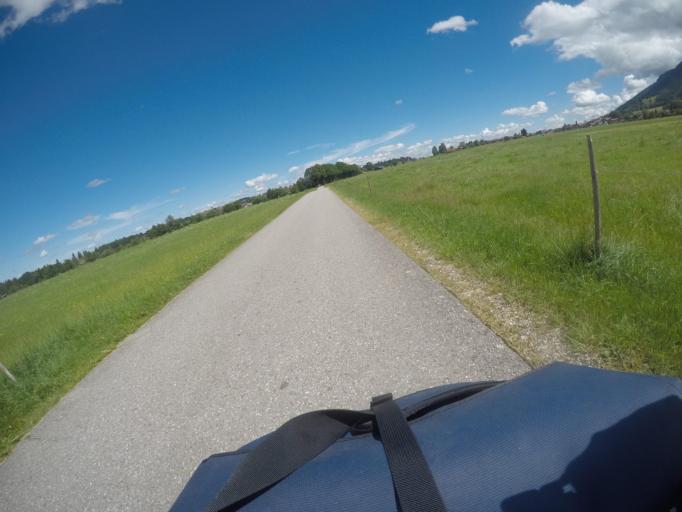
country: DE
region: Bavaria
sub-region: Swabia
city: Halblech
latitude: 47.6164
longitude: 10.7990
